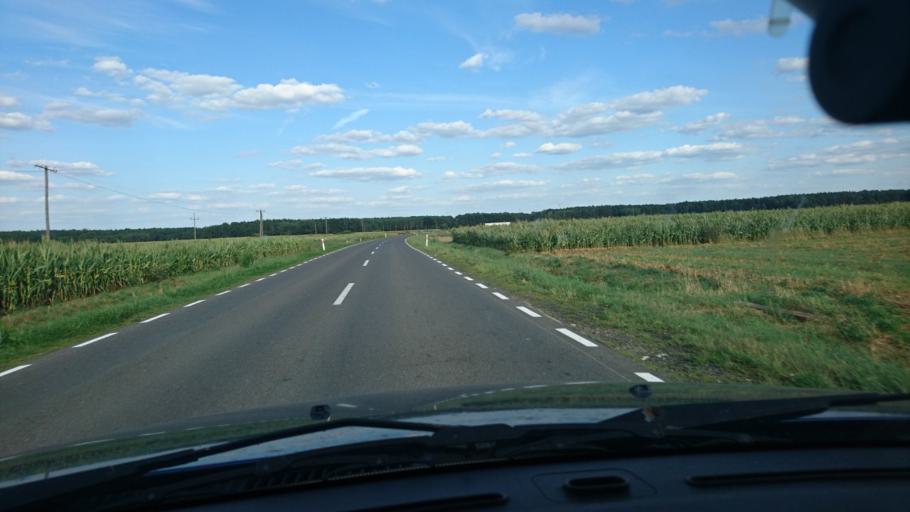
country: PL
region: Greater Poland Voivodeship
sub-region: Powiat krotoszynski
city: Sulmierzyce
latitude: 51.6050
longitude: 17.5599
